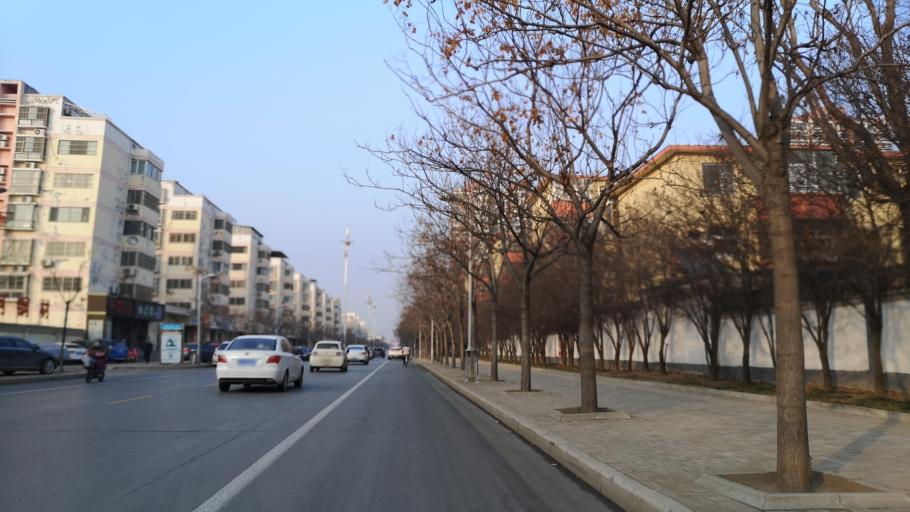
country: CN
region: Henan Sheng
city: Zhongyuanlu
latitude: 35.7707
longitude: 115.0640
